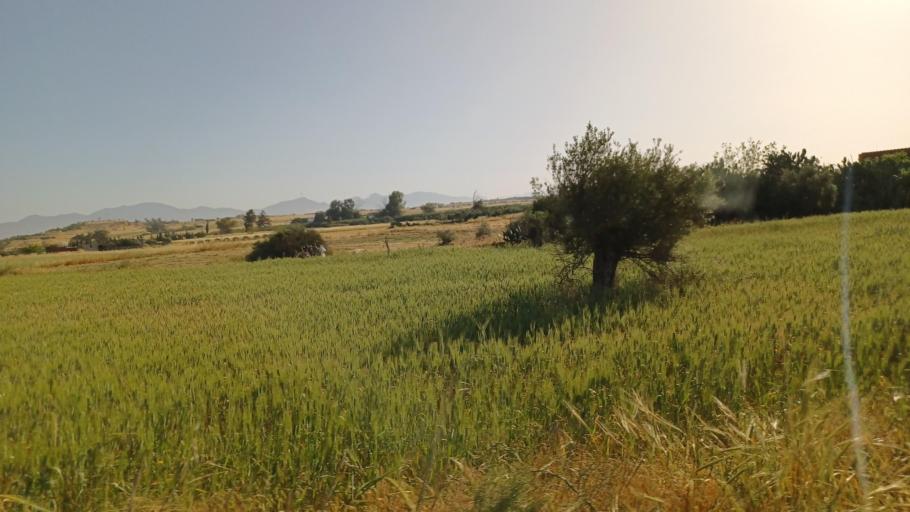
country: CY
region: Lefkosia
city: Mammari
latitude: 35.1614
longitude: 33.2470
